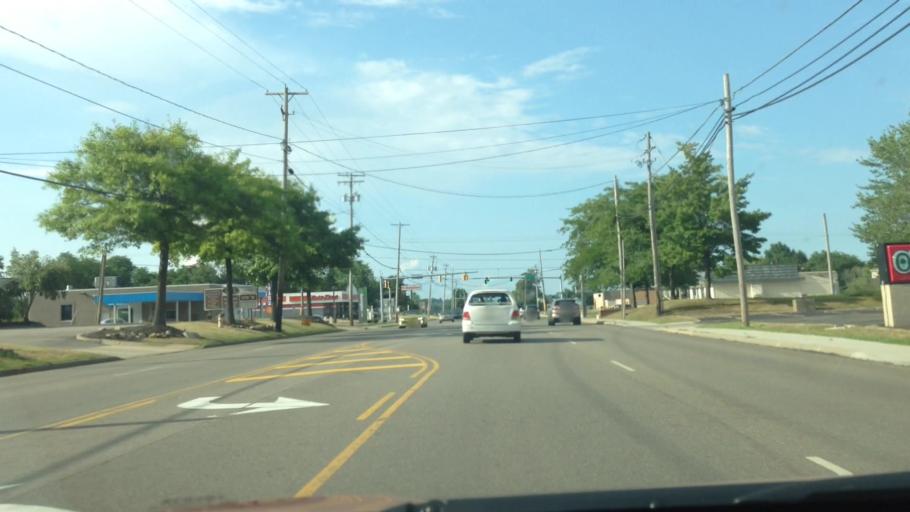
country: US
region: Ohio
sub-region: Summit County
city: Portage Lakes
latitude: 40.9961
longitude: -81.4922
